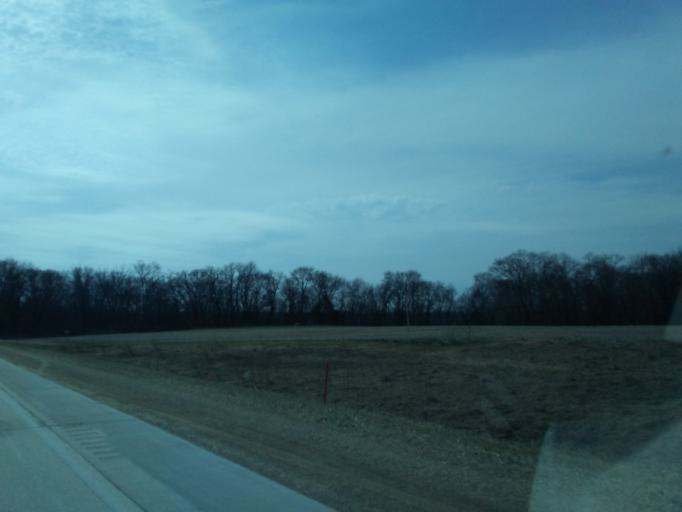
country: US
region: Iowa
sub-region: Winneshiek County
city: Decorah
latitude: 43.3438
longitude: -91.8086
